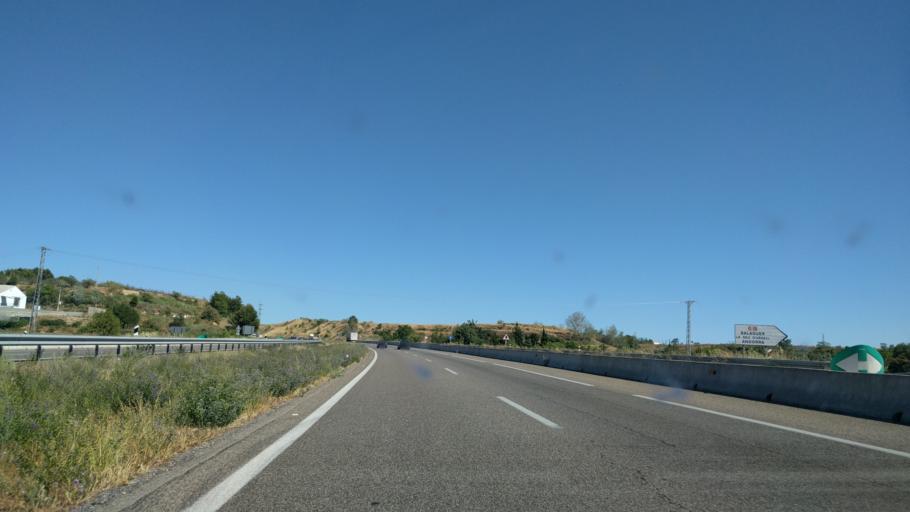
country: ES
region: Catalonia
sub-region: Provincia de Lleida
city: Alcoletge
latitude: 41.6409
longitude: 0.6762
